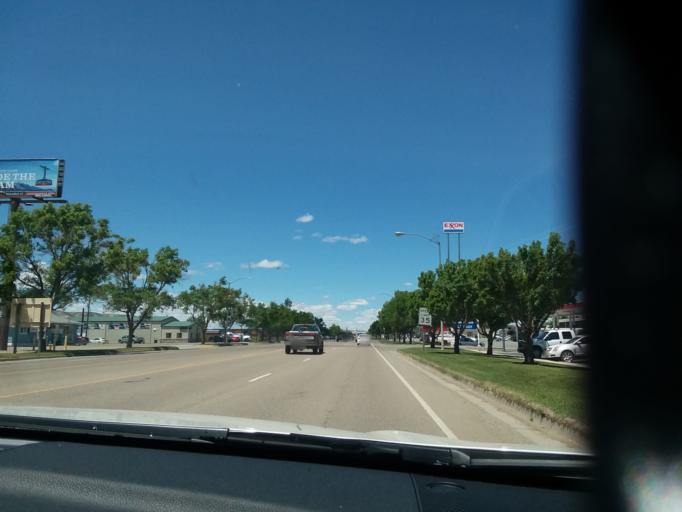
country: US
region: Wyoming
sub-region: Sweetwater County
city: Rock Springs
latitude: 41.6123
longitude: -109.2305
